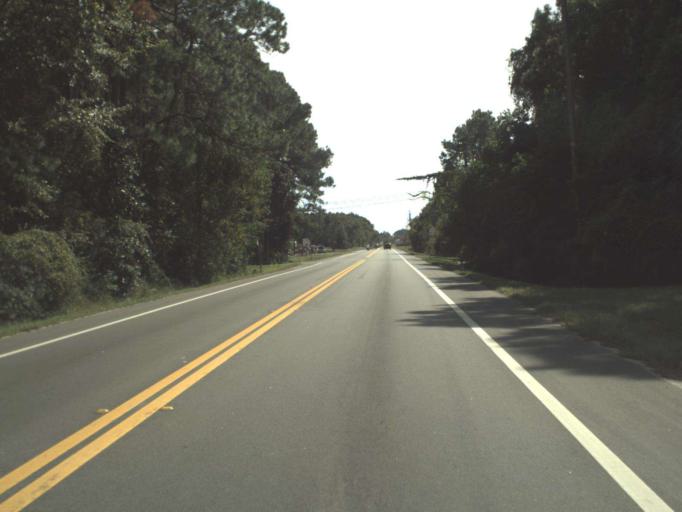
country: US
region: Florida
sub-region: Bay County
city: Hiland Park
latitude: 30.1923
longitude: -85.6250
